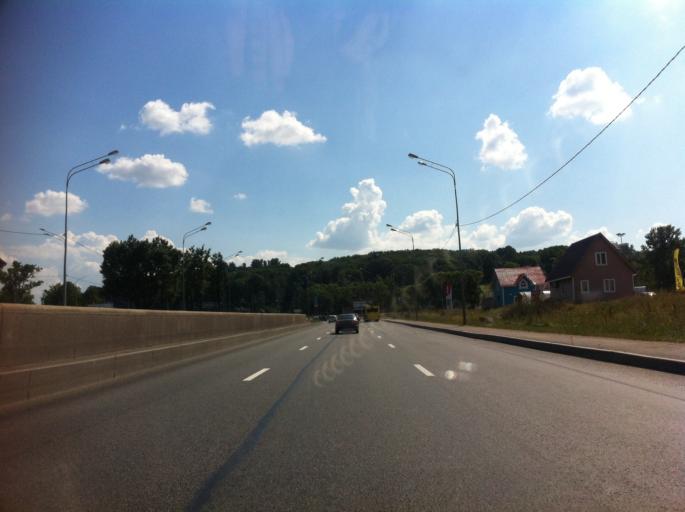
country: RU
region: St.-Petersburg
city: Aleksandrovskaya
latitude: 59.7794
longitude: 30.3249
